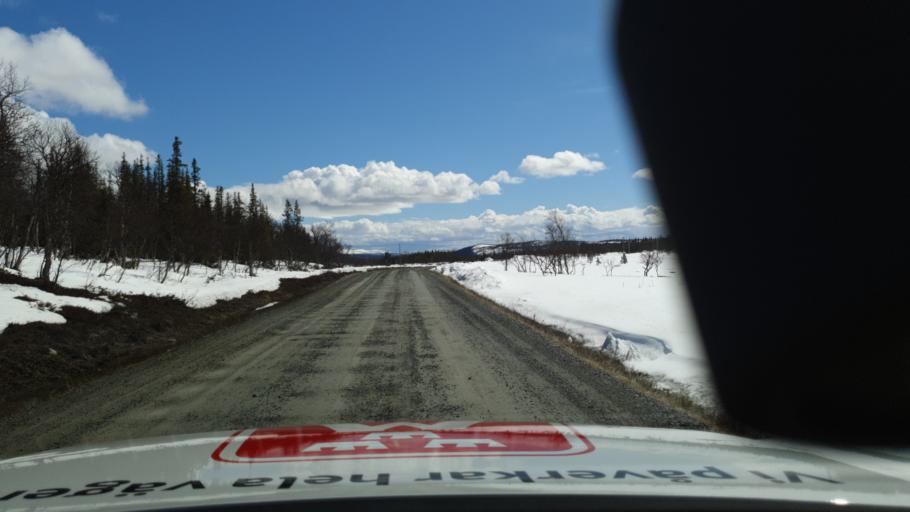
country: SE
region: Jaemtland
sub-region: Are Kommun
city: Are
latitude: 62.8863
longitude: 12.7216
